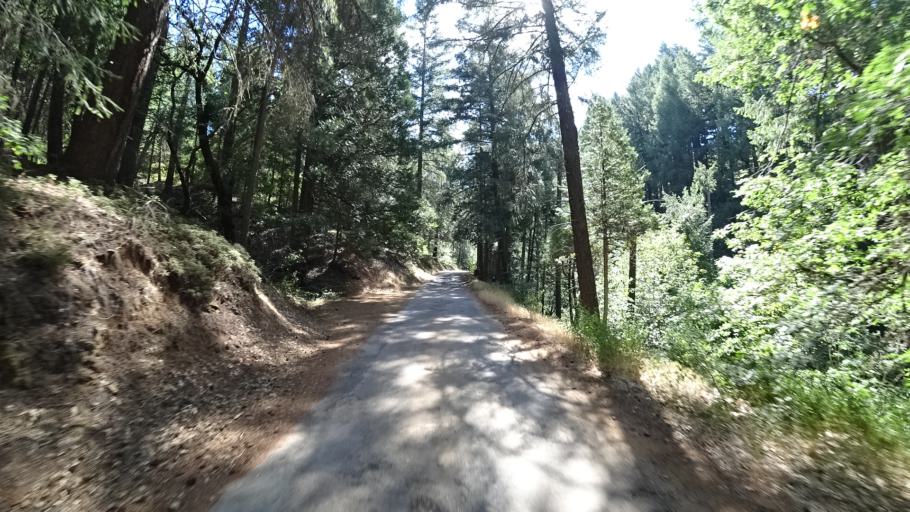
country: US
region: California
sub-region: Amador County
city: Pioneer
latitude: 38.3690
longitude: -120.4470
